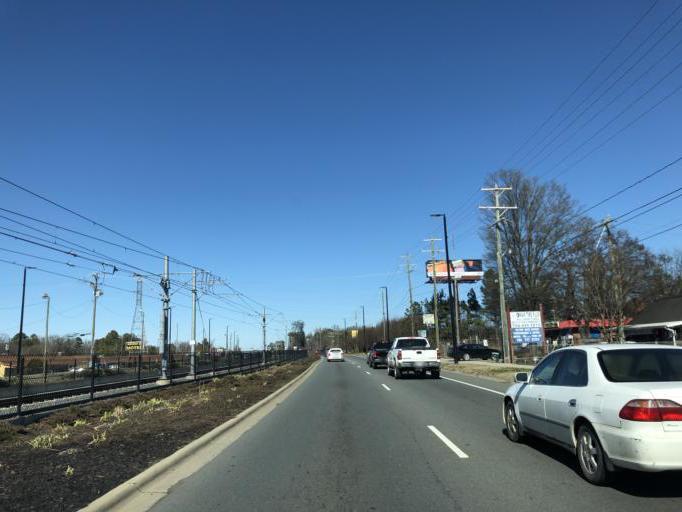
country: US
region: North Carolina
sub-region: Mecklenburg County
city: Charlotte
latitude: 35.2665
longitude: -80.7687
